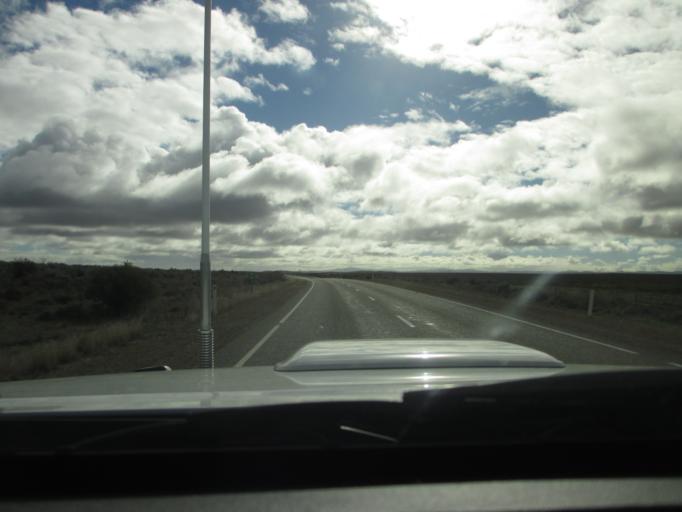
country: AU
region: South Australia
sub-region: Flinders Ranges
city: Quorn
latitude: -32.1830
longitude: 138.5378
